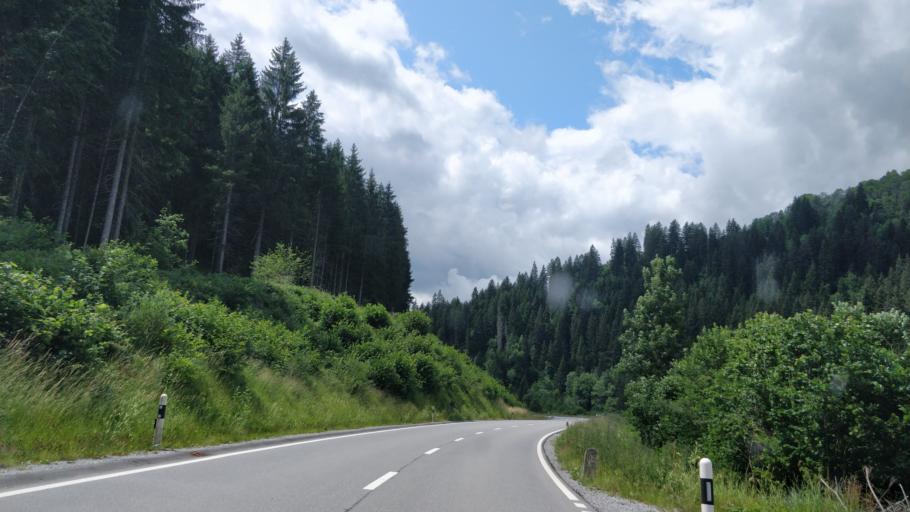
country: CH
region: Grisons
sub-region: Surselva District
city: Ilanz
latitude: 46.7259
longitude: 9.2069
